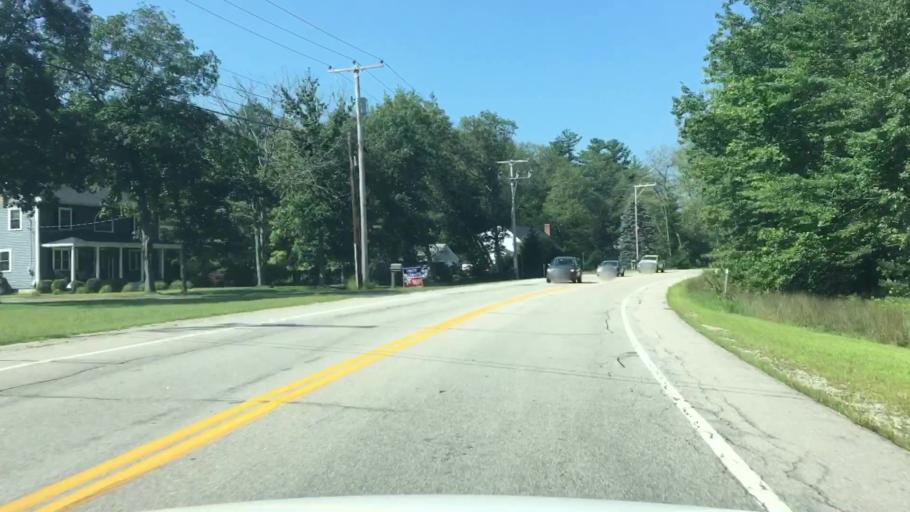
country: US
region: New Hampshire
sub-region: Rockingham County
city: Kingston
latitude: 42.9111
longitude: -71.0729
